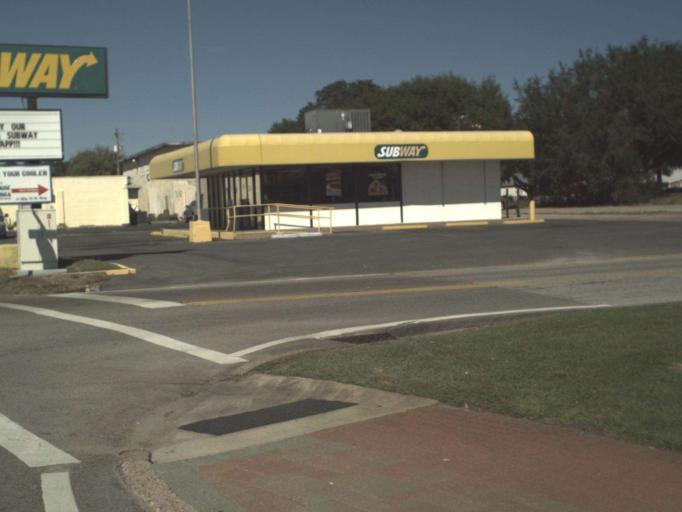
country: US
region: Florida
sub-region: Okaloosa County
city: Fort Walton Beach
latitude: 30.4202
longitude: -86.6096
